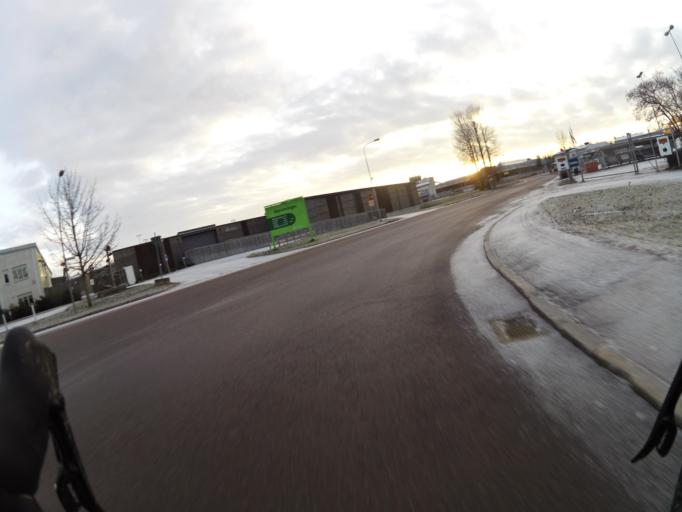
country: SE
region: Gaevleborg
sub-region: Gavle Kommun
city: Gavle
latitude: 60.6609
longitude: 17.1792
